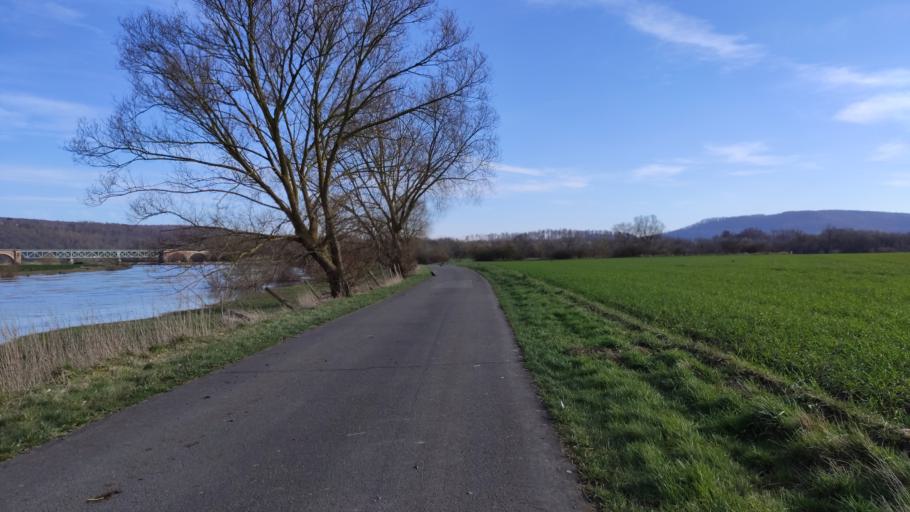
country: DE
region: Lower Saxony
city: Boffzen
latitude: 51.7412
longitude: 9.3748
